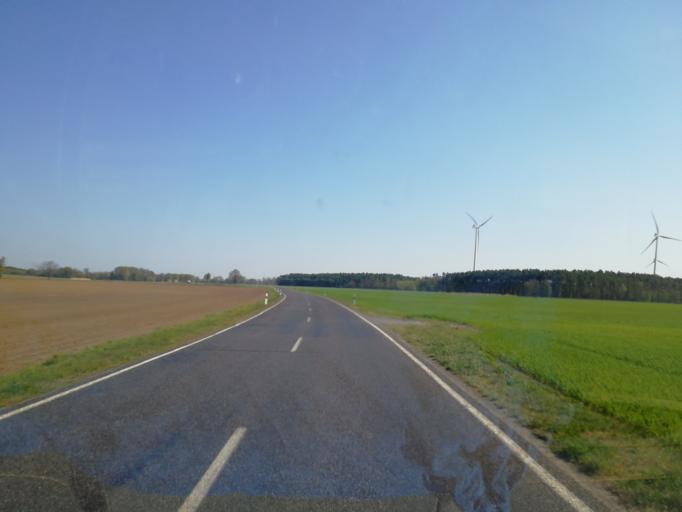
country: DE
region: Brandenburg
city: Crinitz
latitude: 51.7431
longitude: 13.8532
